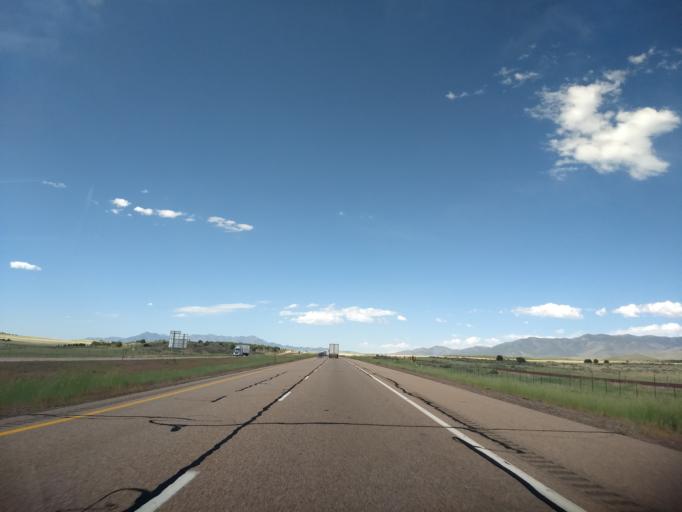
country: US
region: Utah
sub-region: Millard County
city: Fillmore
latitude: 39.0066
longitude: -112.3118
